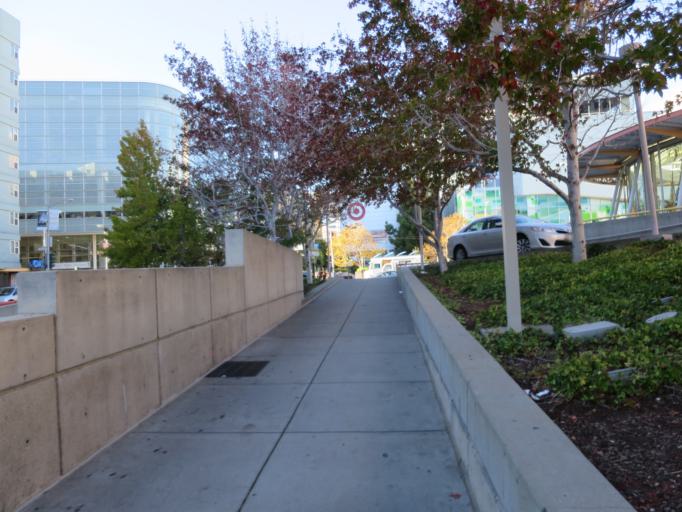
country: US
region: California
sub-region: San Francisco County
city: San Francisco
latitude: 37.7830
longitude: -122.4021
